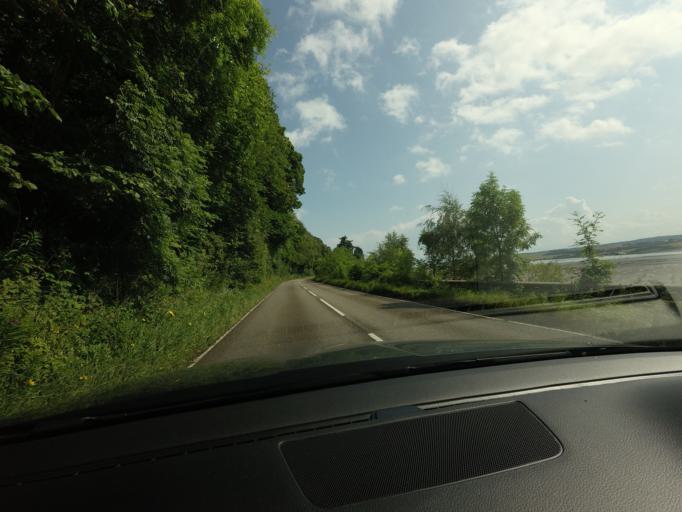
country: GB
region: Scotland
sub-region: Highland
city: Dingwall
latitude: 57.6146
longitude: -4.3986
